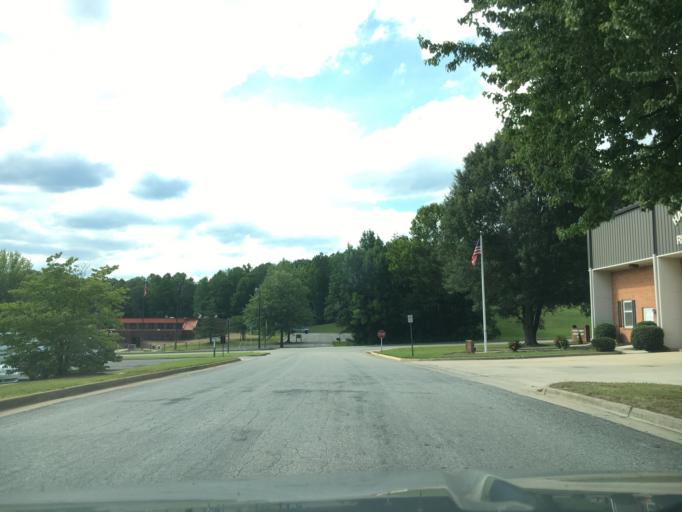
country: US
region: Virginia
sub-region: Halifax County
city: South Boston
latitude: 36.7164
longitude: -78.9091
